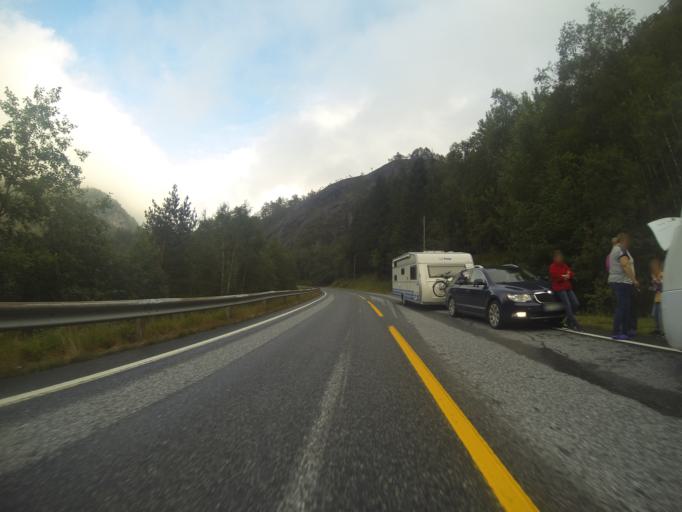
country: NO
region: Rogaland
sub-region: Sauda
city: Sauda
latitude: 59.8741
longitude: 6.4000
